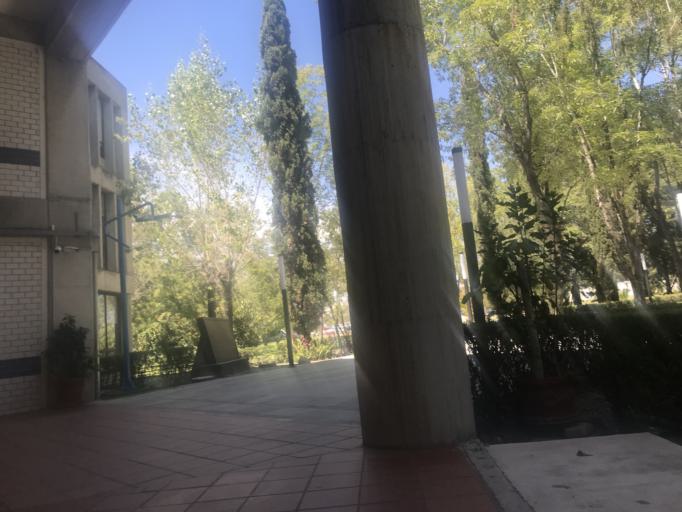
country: MX
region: Puebla
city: Puebla
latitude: 19.0319
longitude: -98.2415
